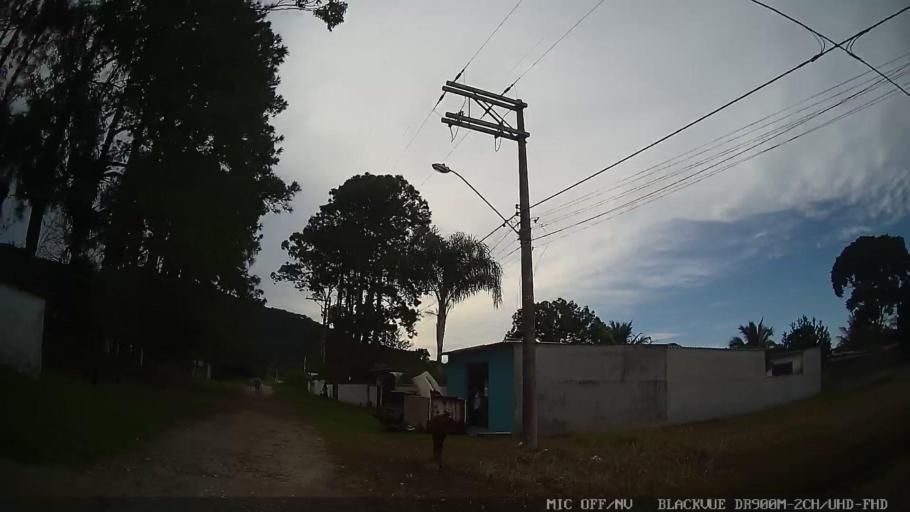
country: BR
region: Sao Paulo
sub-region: Iguape
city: Iguape
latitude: -24.6842
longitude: -47.4694
